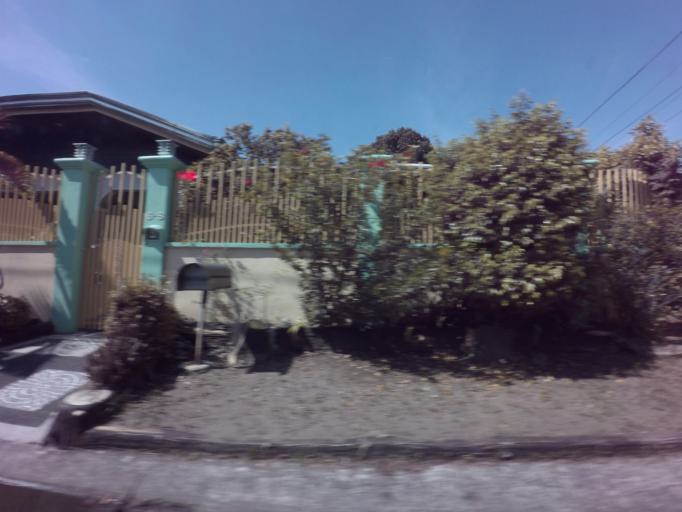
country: PH
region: Calabarzon
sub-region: Province of Rizal
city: Las Pinas
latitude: 14.4370
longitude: 120.9912
